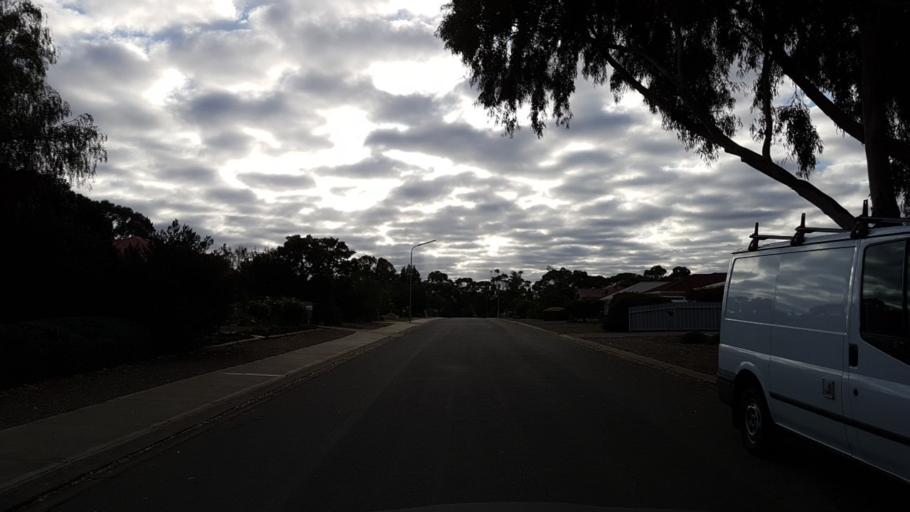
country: AU
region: South Australia
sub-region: Alexandrina
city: Strathalbyn
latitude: -35.2627
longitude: 138.8993
